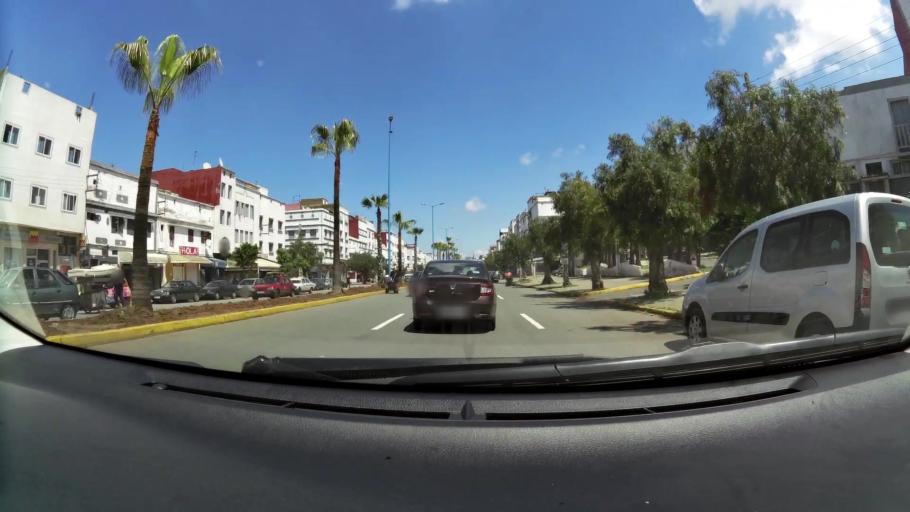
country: MA
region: Grand Casablanca
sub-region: Casablanca
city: Casablanca
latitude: 33.5616
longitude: -7.5727
